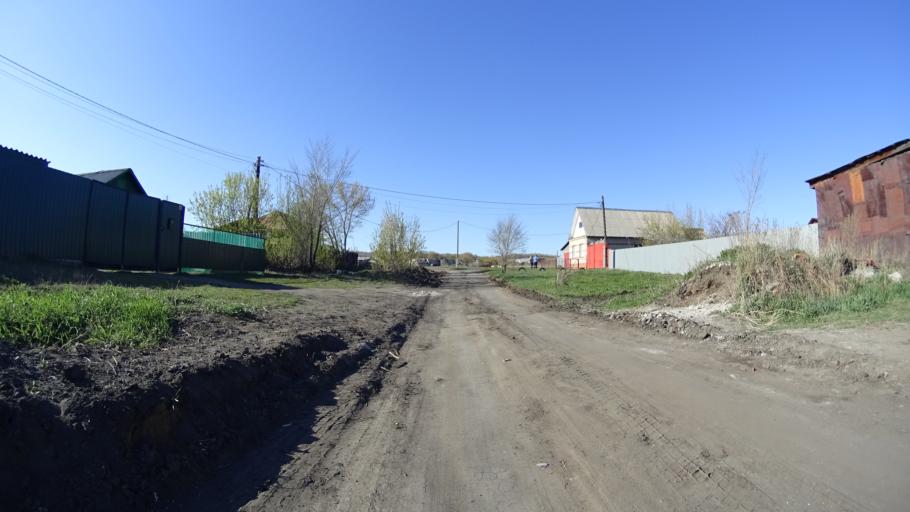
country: RU
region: Chelyabinsk
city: Troitsk
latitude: 54.0934
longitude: 61.5998
